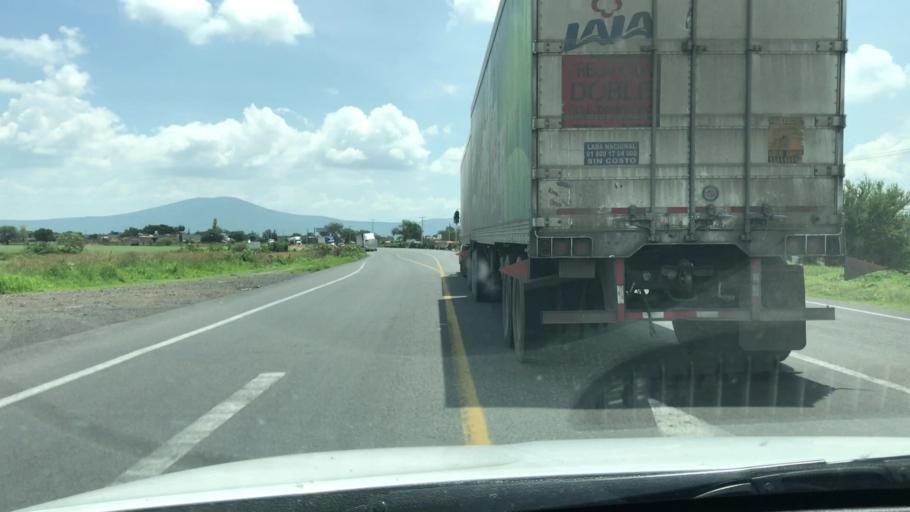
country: MX
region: Michoacan
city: Tanhuato de Guerrero
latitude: 20.2844
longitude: -102.3413
